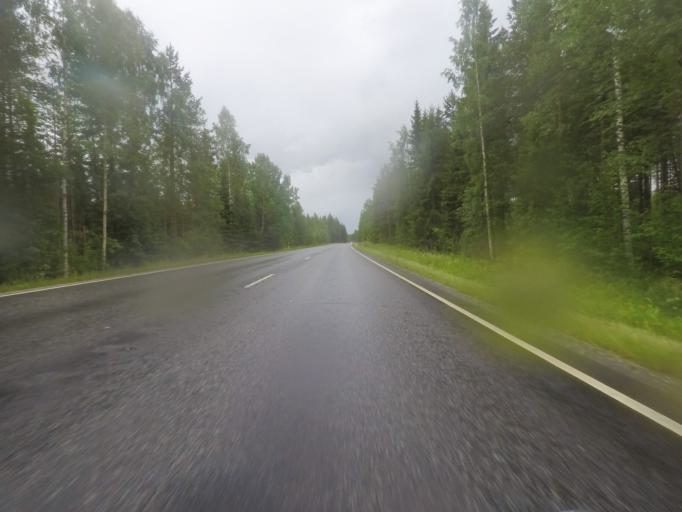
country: FI
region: Central Finland
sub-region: Jyvaeskylae
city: Toivakka
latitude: 62.2107
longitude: 26.2098
